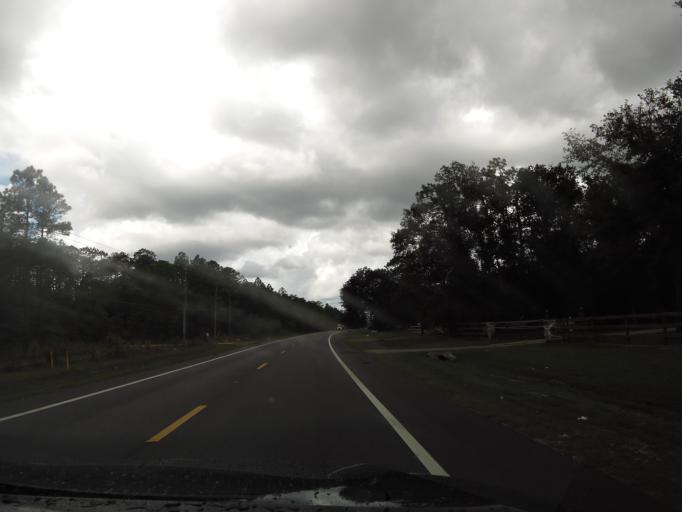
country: US
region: Florida
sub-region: Clay County
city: Asbury Lake
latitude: 30.0338
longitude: -81.8243
